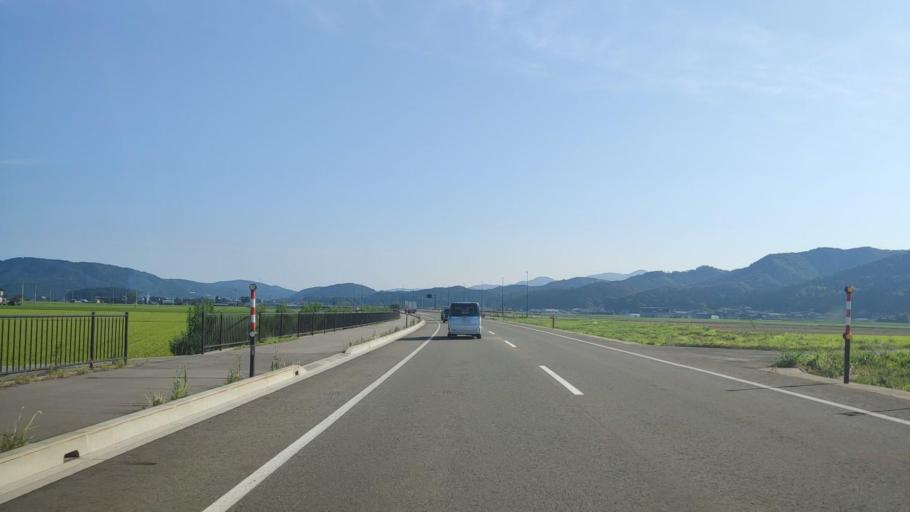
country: JP
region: Fukui
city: Maruoka
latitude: 36.1787
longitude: 136.2670
